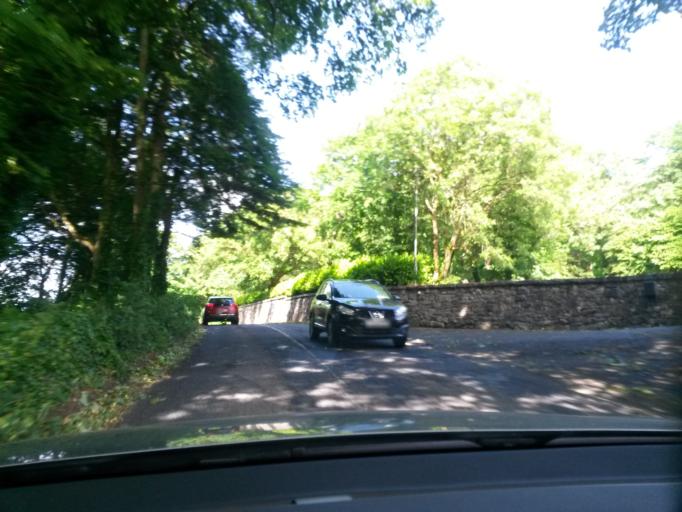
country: IE
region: Munster
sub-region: An Clar
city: Ennis
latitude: 52.9772
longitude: -9.1058
